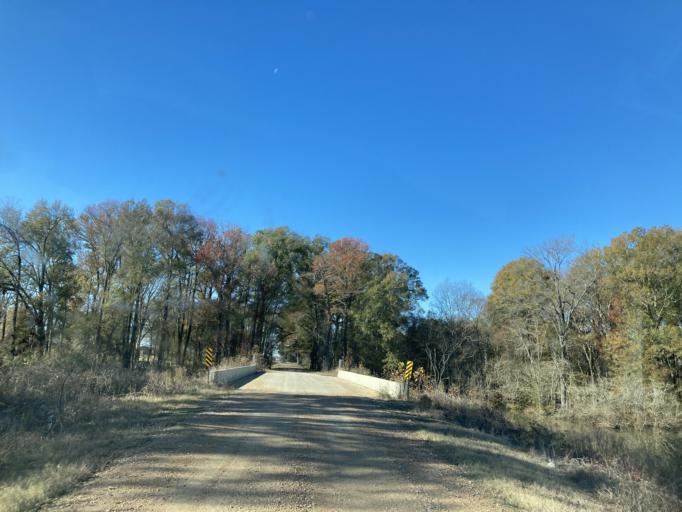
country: US
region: Mississippi
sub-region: Sharkey County
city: Rolling Fork
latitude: 32.8498
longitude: -90.6959
